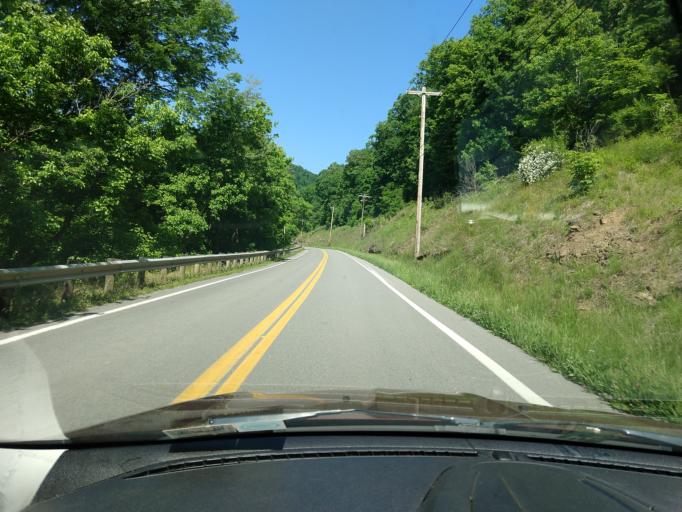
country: US
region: West Virginia
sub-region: Gilmer County
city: Glenville
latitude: 38.8796
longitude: -80.7137
